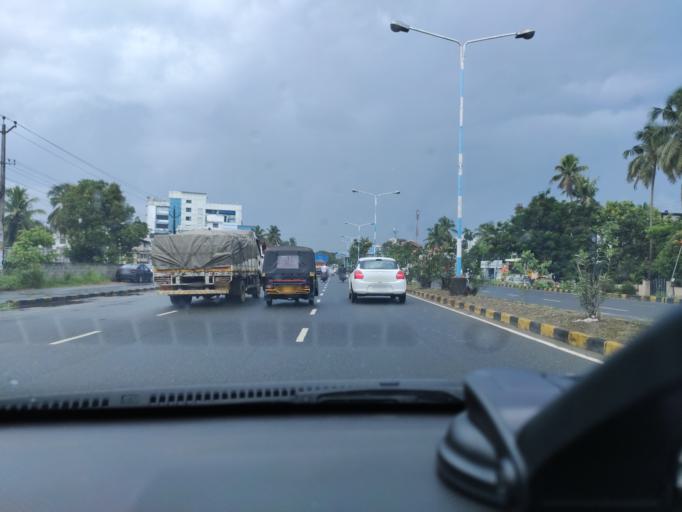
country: IN
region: Kerala
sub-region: Ernakulam
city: Cochin
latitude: 9.9612
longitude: 76.3185
